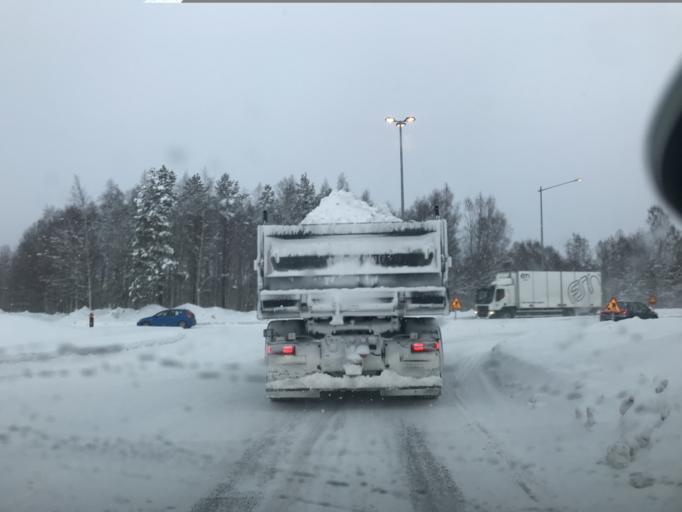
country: SE
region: Norrbotten
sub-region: Lulea Kommun
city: Lulea
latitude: 65.6126
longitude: 22.1346
